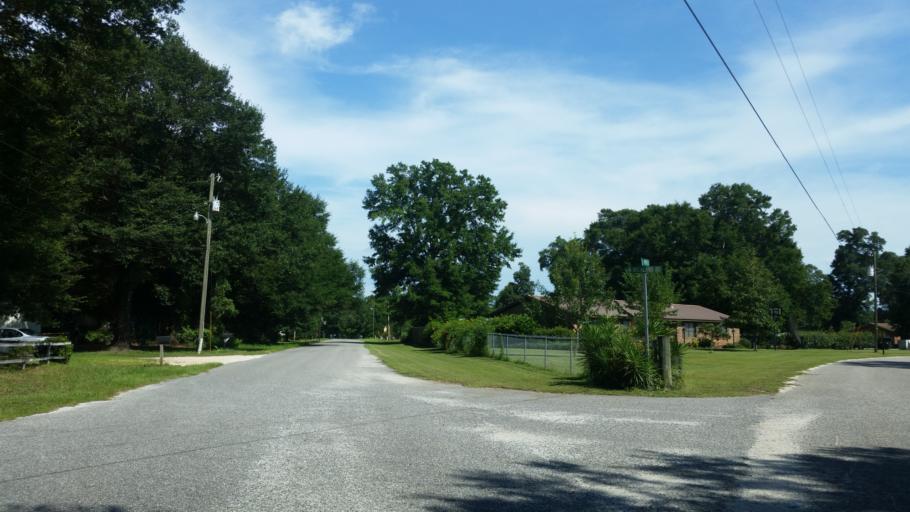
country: US
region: Florida
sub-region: Santa Rosa County
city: Pace
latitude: 30.5948
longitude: -87.1472
